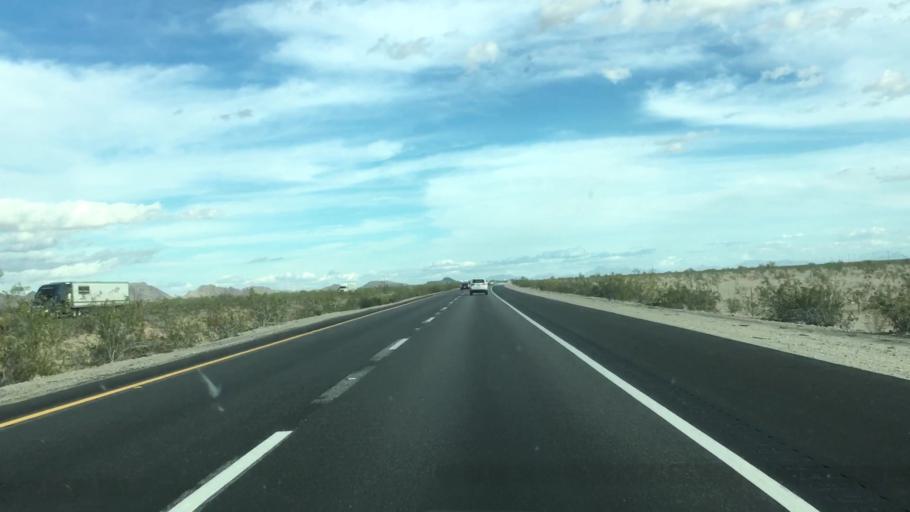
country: US
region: California
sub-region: Riverside County
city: Mesa Verde
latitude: 33.6095
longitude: -114.8434
